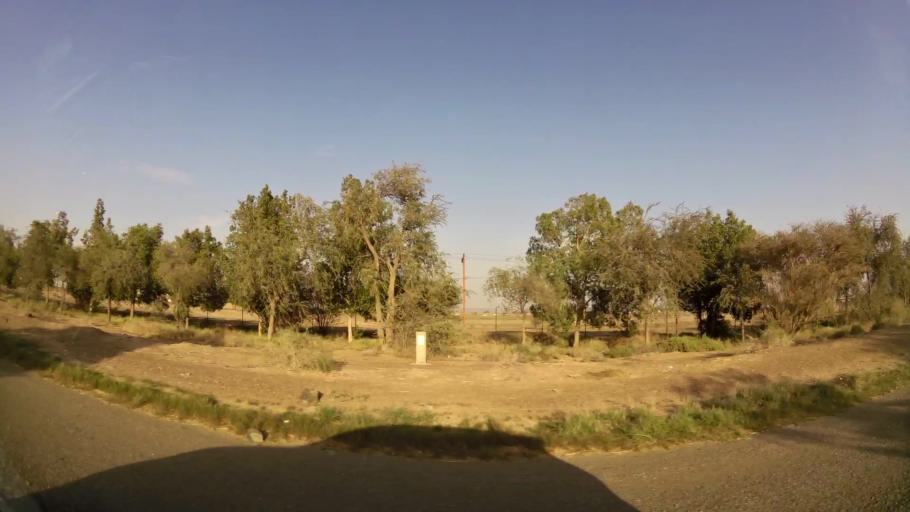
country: AE
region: Abu Dhabi
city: Al Ain
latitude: 24.1161
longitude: 55.8243
